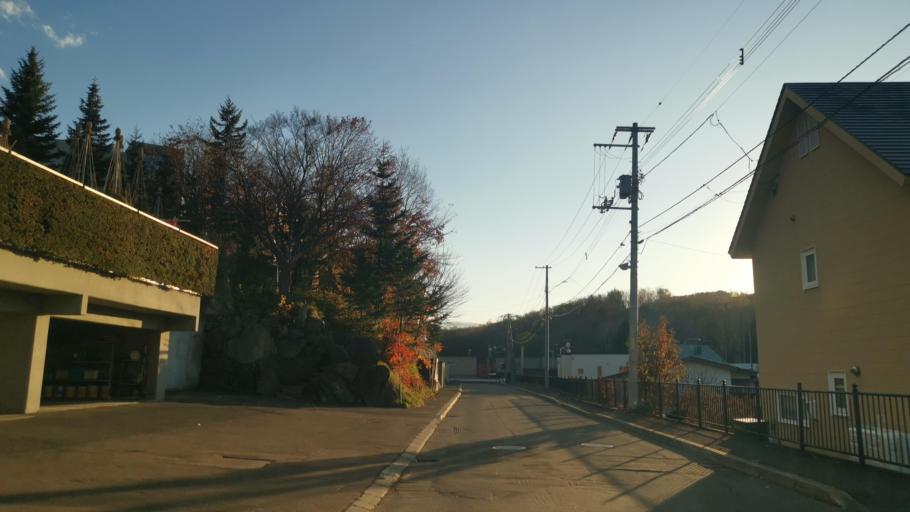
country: JP
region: Hokkaido
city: Sapporo
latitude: 42.9989
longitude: 141.3663
